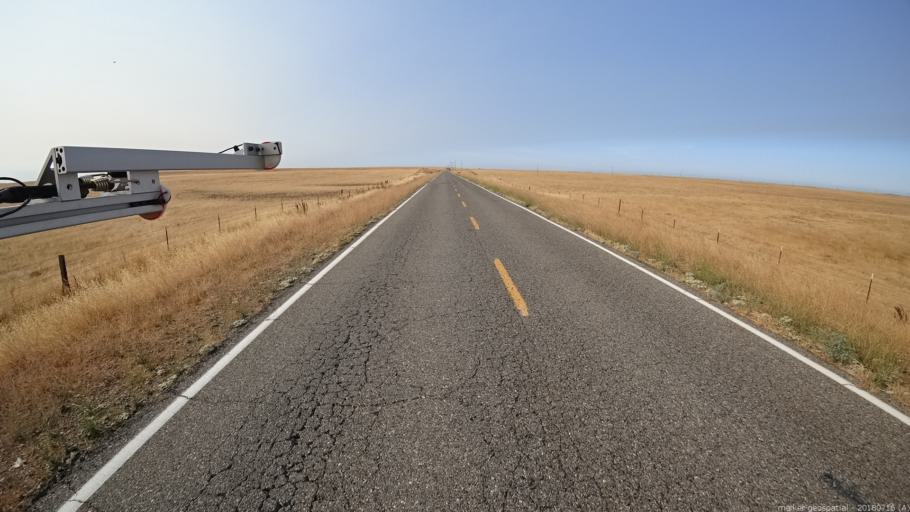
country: US
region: California
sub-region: Madera County
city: Madera Acres
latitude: 37.1319
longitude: -120.0203
